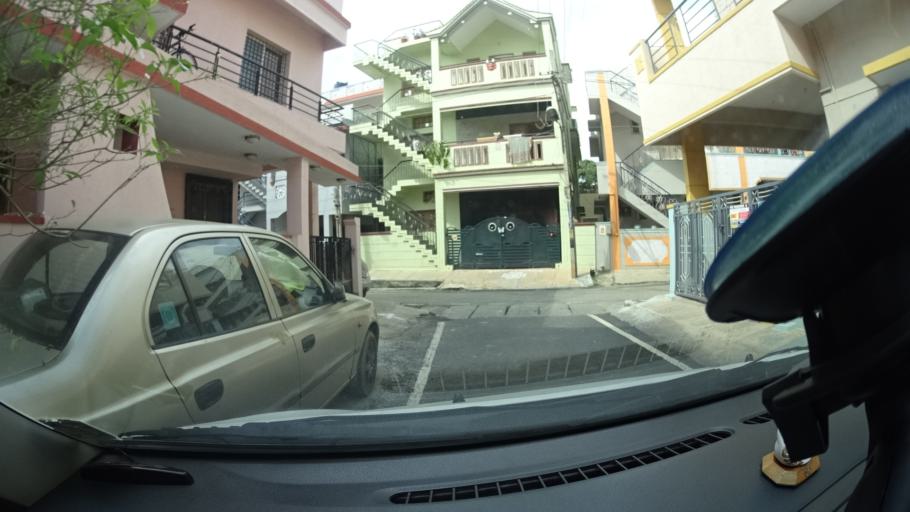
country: IN
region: Karnataka
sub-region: Bangalore Urban
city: Yelahanka
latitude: 13.0980
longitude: 77.5862
